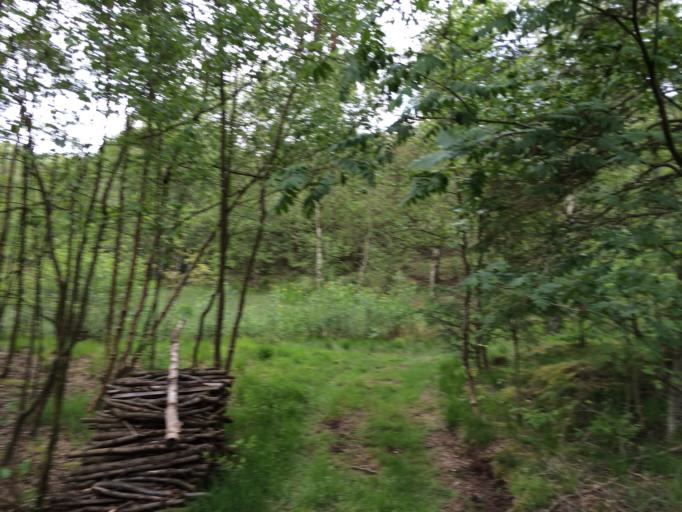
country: DK
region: Central Jutland
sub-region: Holstebro Kommune
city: Ulfborg
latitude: 56.2357
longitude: 8.4183
